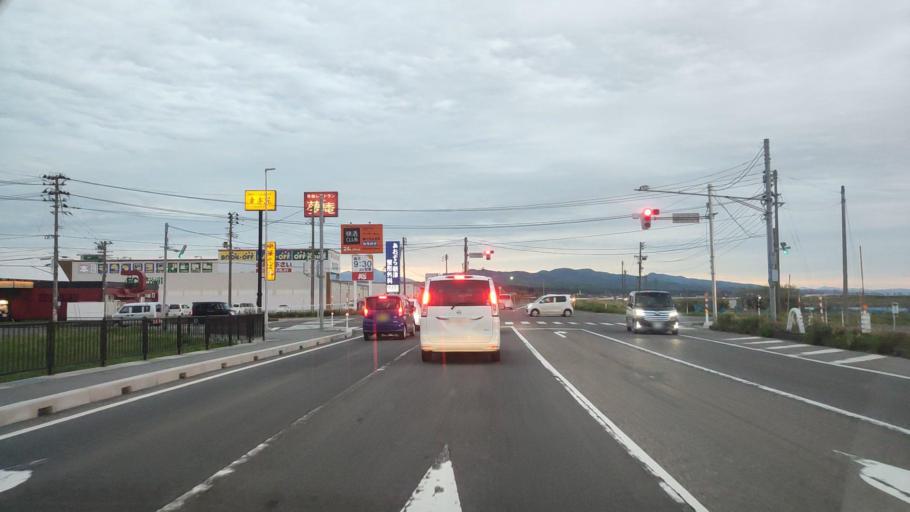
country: JP
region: Niigata
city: Niitsu-honcho
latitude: 37.7868
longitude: 139.1119
